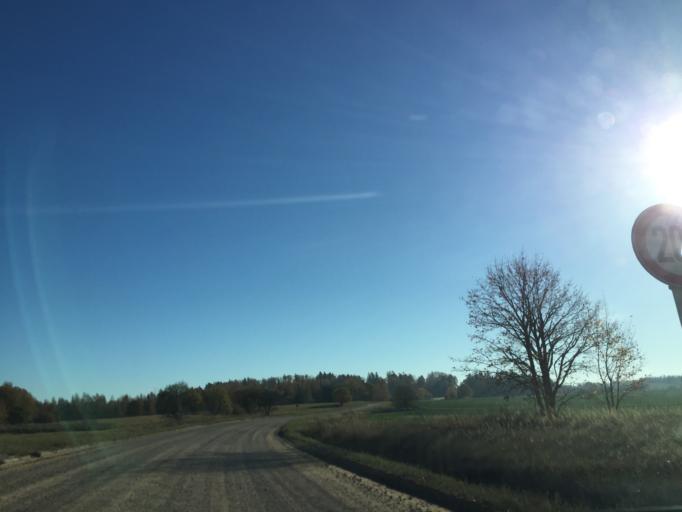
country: LV
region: Tukuma Rajons
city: Tukums
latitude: 56.9677
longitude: 22.9628
